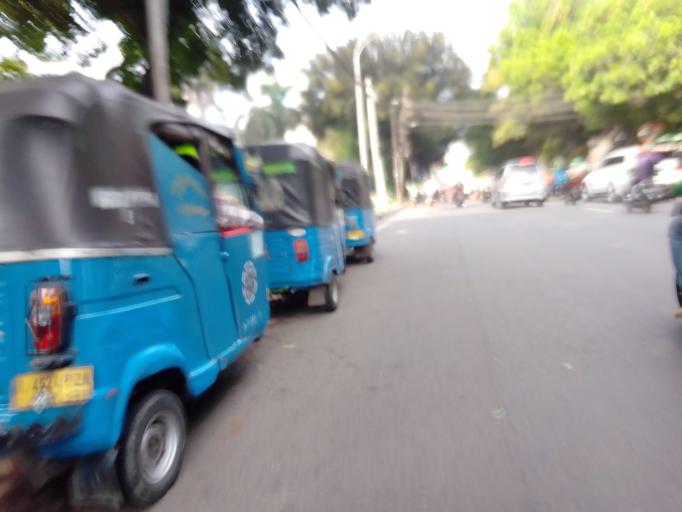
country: ID
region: Jakarta Raya
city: Jakarta
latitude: -6.1828
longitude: 106.8303
